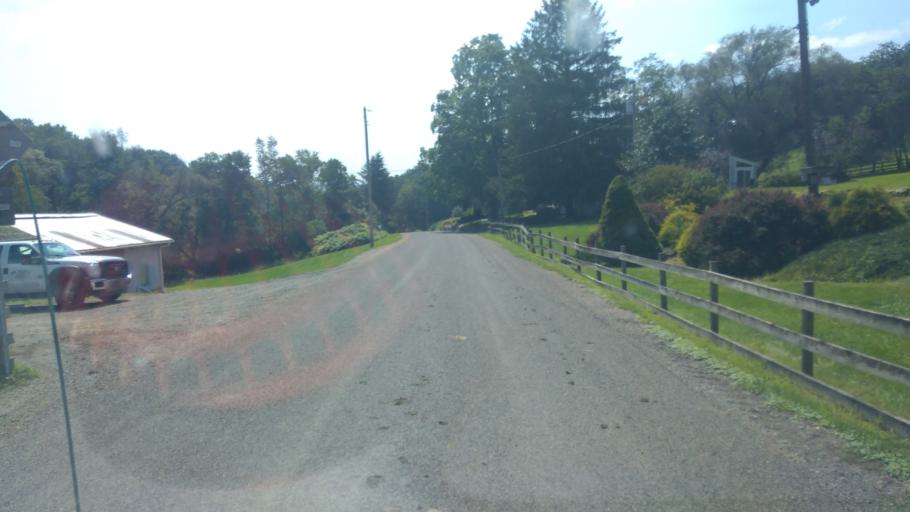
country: US
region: New York
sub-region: Steuben County
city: Canisteo
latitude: 42.3194
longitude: -77.6019
